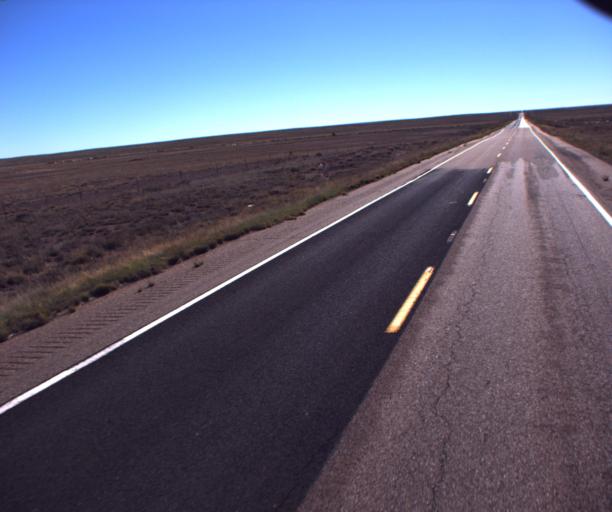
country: US
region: Arizona
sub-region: Navajo County
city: Snowflake
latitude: 34.7647
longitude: -109.8155
